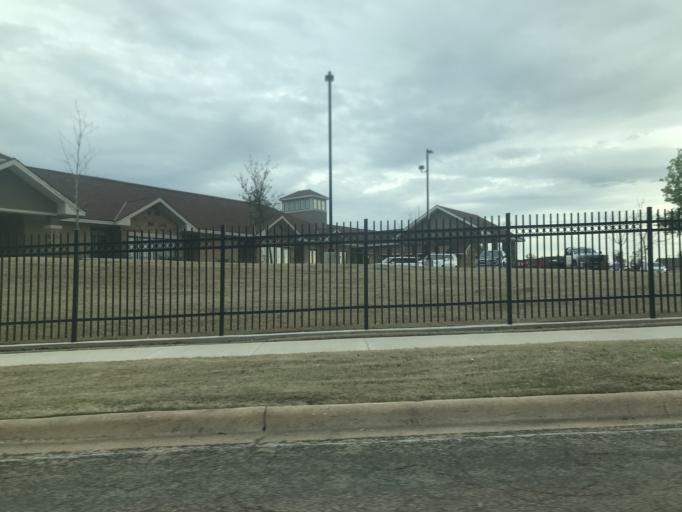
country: US
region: Texas
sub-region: Taylor County
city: Abilene
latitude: 32.4686
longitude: -99.7299
